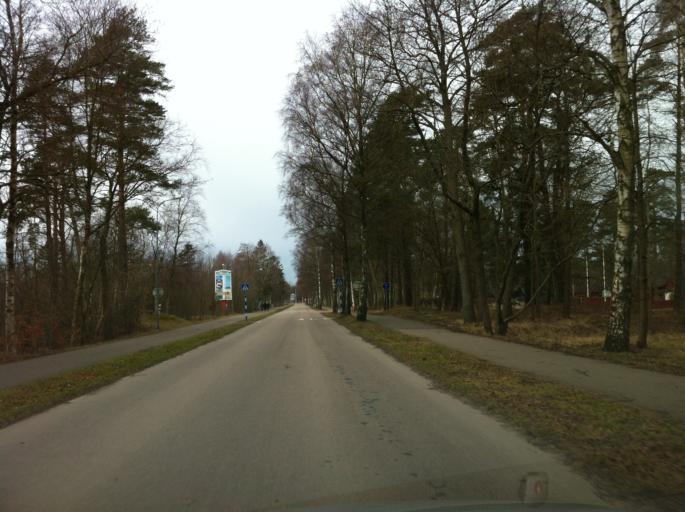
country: SE
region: Skane
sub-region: Angelholms Kommun
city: AEngelholm
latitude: 56.2533
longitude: 12.8411
